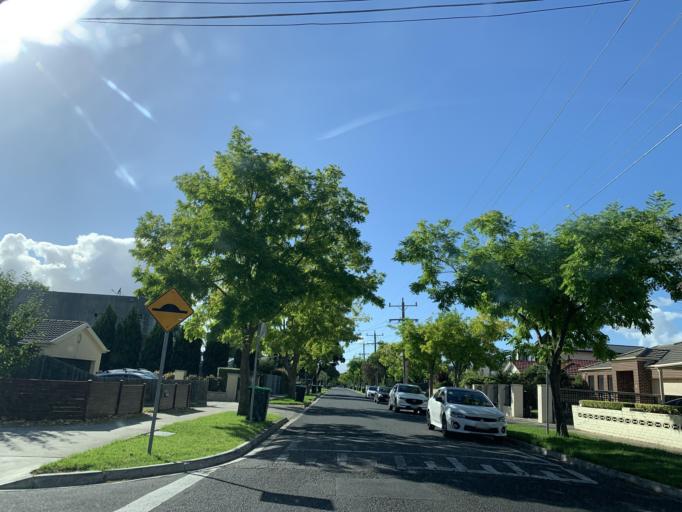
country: AU
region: Victoria
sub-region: Moreland
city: Oak Park
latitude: -37.7255
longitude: 144.9166
